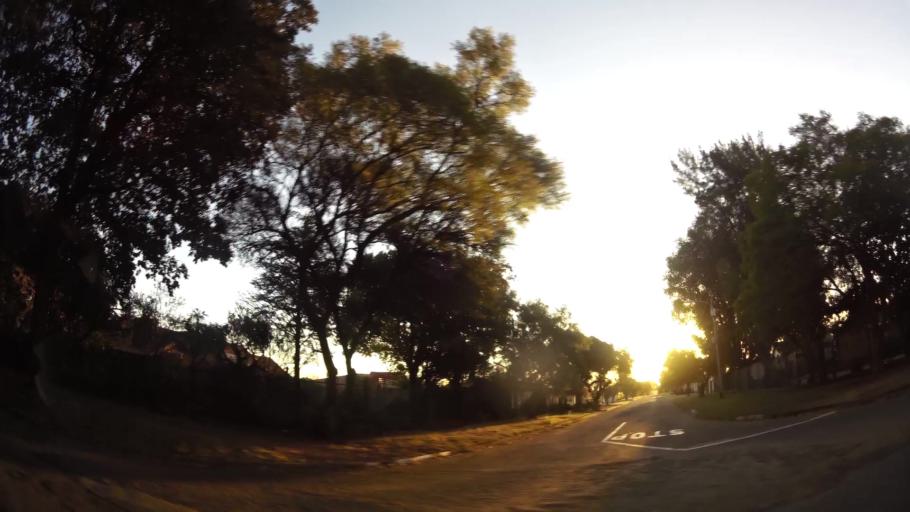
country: ZA
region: Gauteng
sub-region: City of Johannesburg Metropolitan Municipality
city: Roodepoort
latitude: -26.1491
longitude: 27.8819
